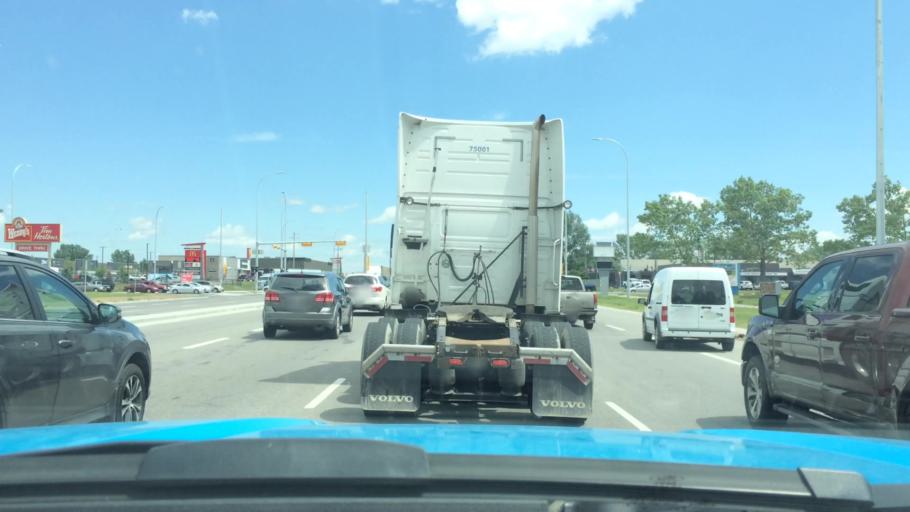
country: CA
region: Alberta
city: Calgary
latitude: 51.0960
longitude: -114.0352
